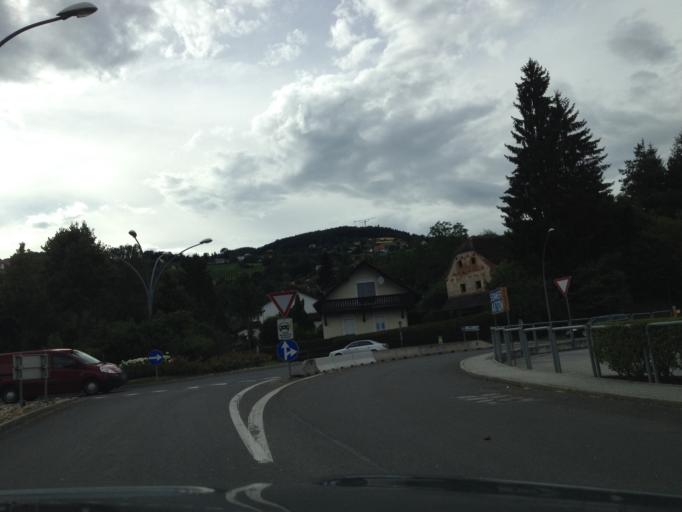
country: AT
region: Styria
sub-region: Politischer Bezirk Hartberg-Fuerstenfeld
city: Hartberg
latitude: 47.2833
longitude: 15.9771
